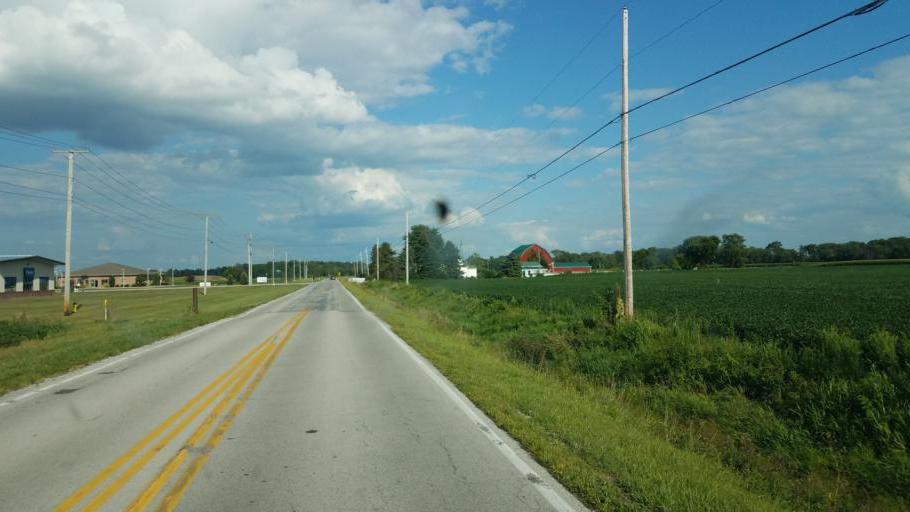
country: US
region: Ohio
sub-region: Wood County
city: Bowling Green
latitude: 41.3635
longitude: -83.6083
